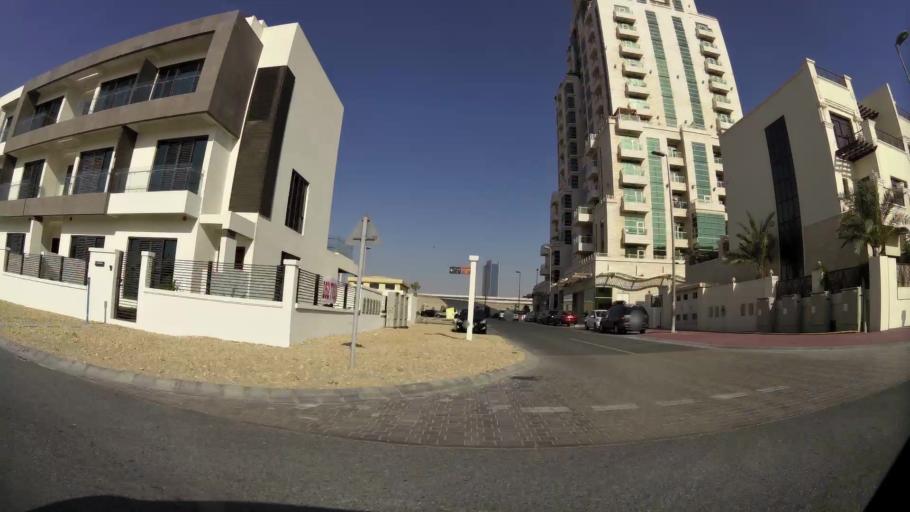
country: AE
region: Dubai
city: Dubai
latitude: 25.0532
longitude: 55.2190
